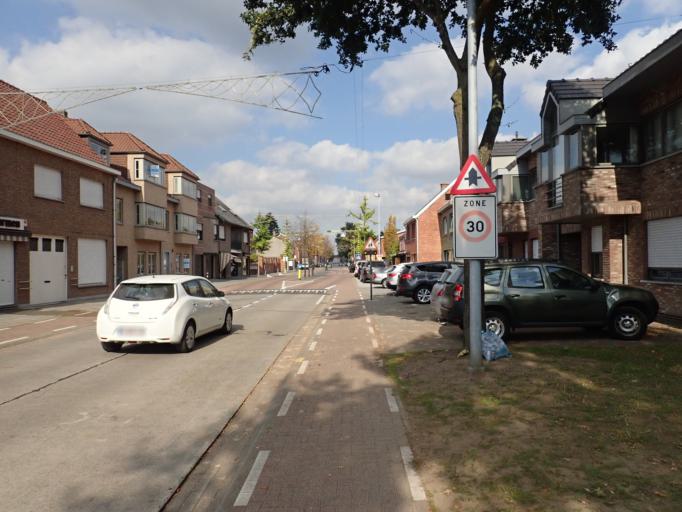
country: BE
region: Flanders
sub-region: Provincie Oost-Vlaanderen
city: Stekene
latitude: 51.2349
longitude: 4.0438
